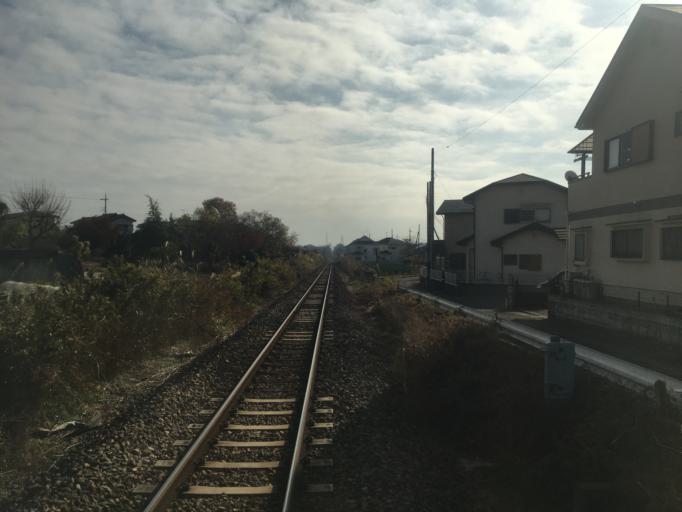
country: JP
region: Saitama
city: Yorii
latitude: 36.1572
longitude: 139.1989
